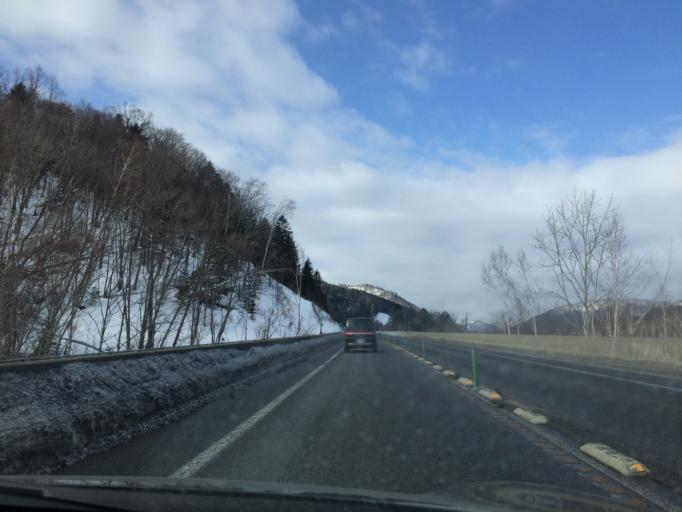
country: JP
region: Hokkaido
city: Shimo-furano
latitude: 43.0529
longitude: 142.6385
